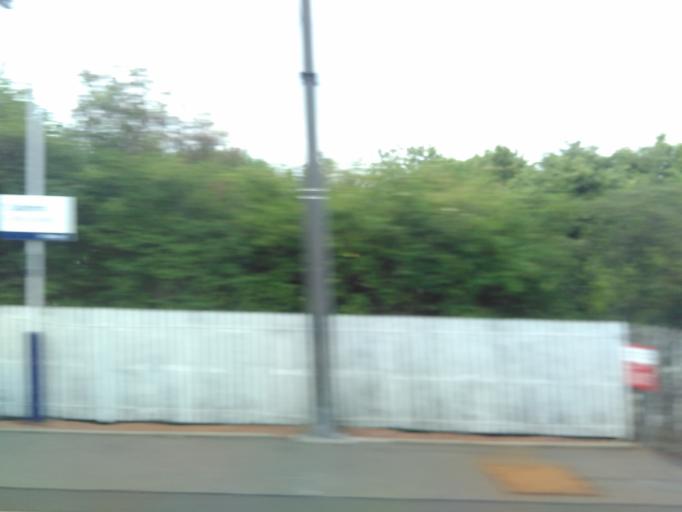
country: GB
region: Scotland
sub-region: Edinburgh
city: Colinton
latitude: 55.9260
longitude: -3.2452
